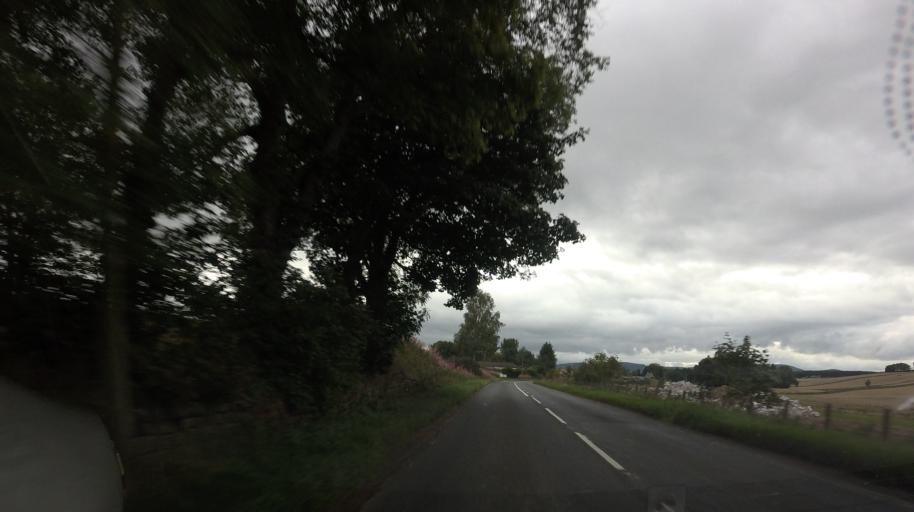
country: GB
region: Scotland
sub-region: Aberdeenshire
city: Kemnay
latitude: 57.1804
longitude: -2.4654
